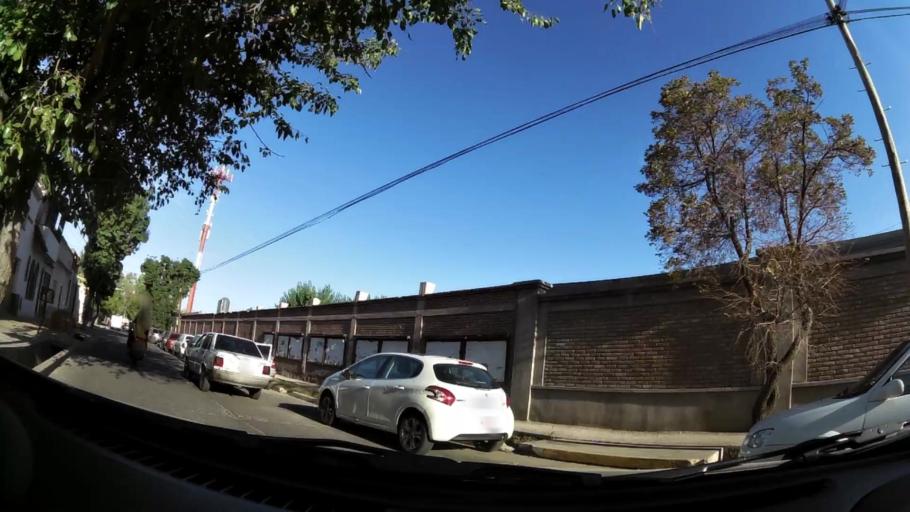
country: AR
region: Mendoza
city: Mendoza
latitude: -32.9074
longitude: -68.8415
